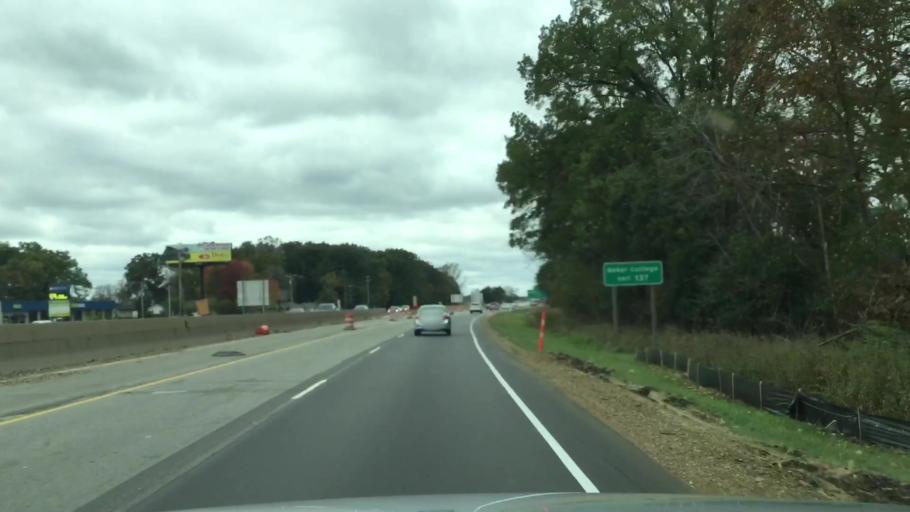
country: US
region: Michigan
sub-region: Jackson County
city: Jackson
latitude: 42.2697
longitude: -84.4367
